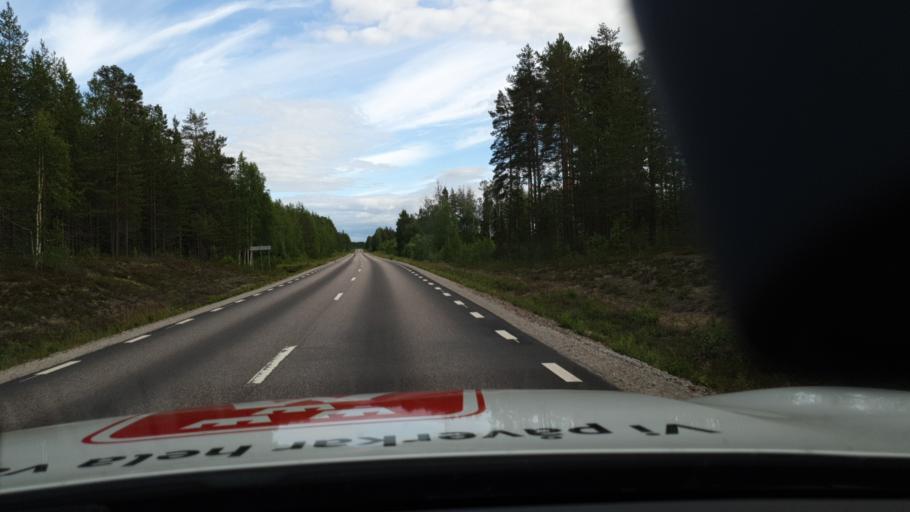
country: SE
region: Norrbotten
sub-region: Overkalix Kommun
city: OEverkalix
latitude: 66.3854
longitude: 22.8262
